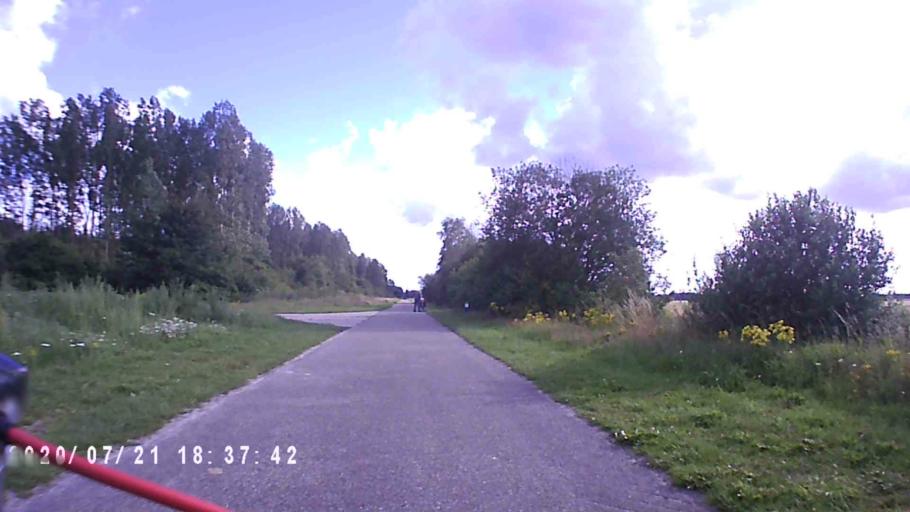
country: NL
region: Groningen
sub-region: Gemeente Hoogezand-Sappemeer
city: Hoogezand
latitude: 53.1953
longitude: 6.7423
